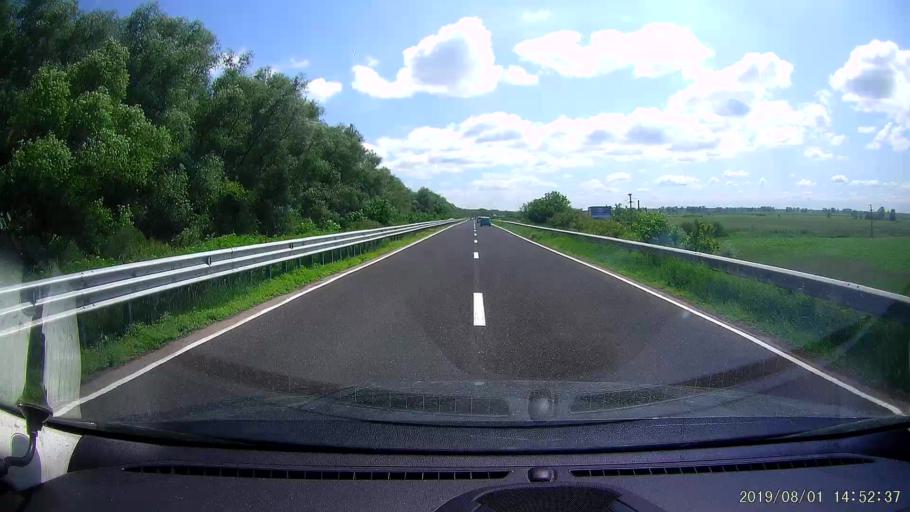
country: RO
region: Braila
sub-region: Comuna Vadeni
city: Vadeni
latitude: 45.3513
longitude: 28.0097
